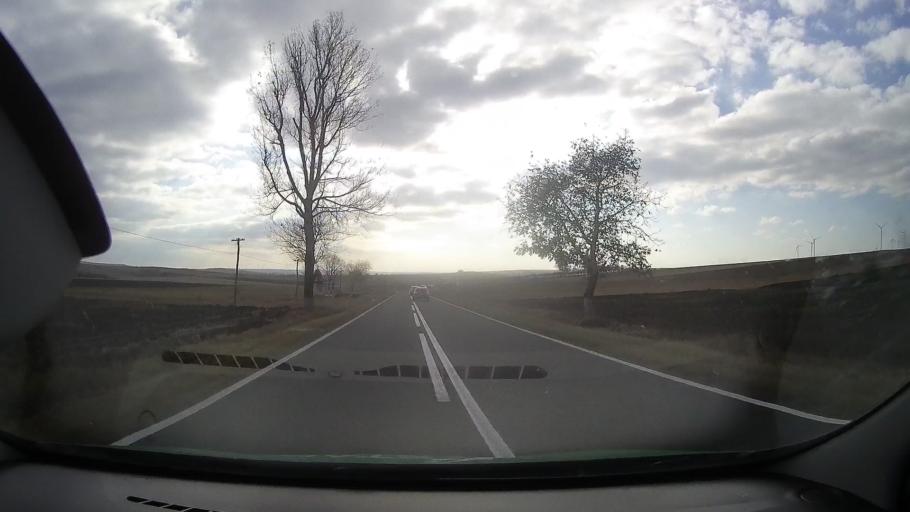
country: RO
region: Tulcea
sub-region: Comuna Topolog
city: Topolog
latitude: 44.8901
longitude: 28.3931
